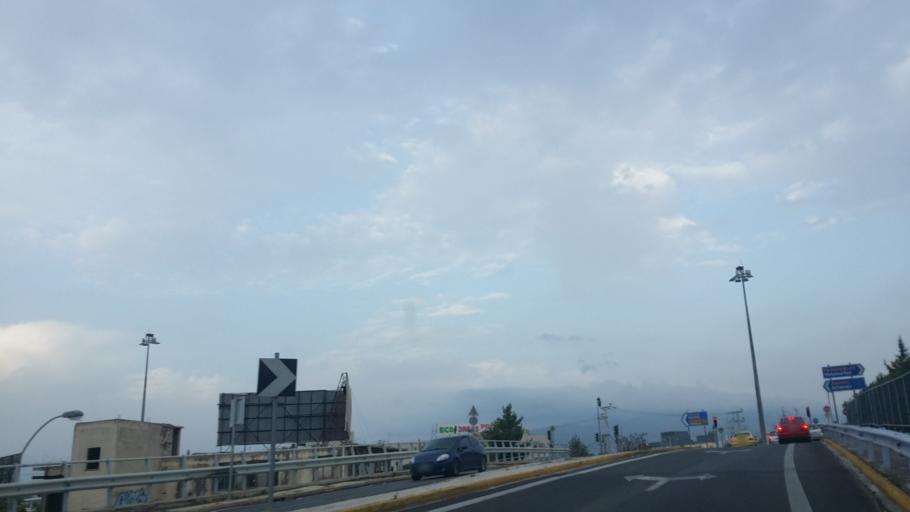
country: GR
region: Attica
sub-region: Nomarchia Athinas
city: Metamorfosi
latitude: 38.0690
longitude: 23.7590
